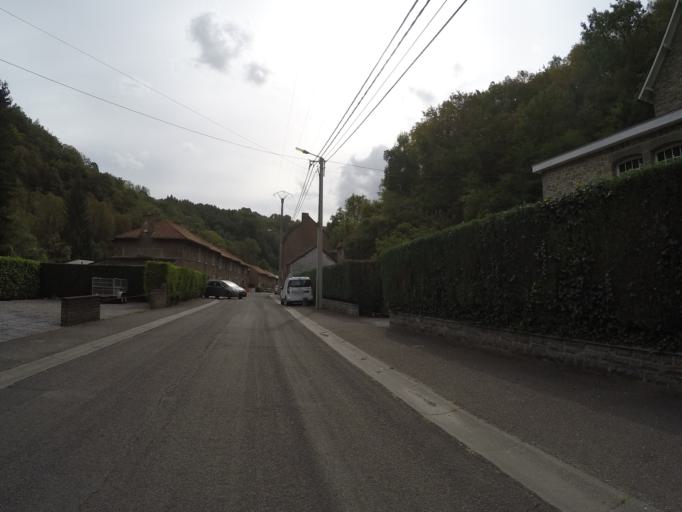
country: BE
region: Wallonia
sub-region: Province de Namur
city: Dinant
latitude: 50.2729
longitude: 4.9187
